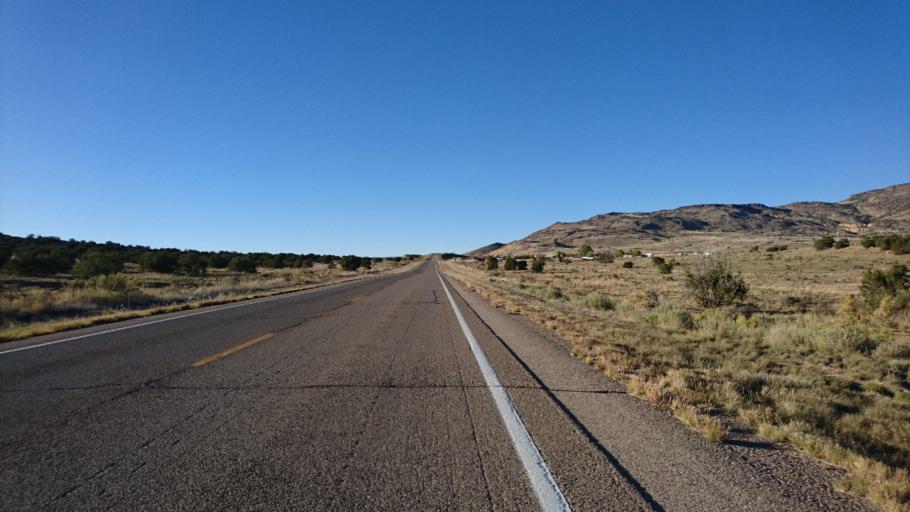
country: US
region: New Mexico
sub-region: Cibola County
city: Grants
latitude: 35.0992
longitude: -107.7748
